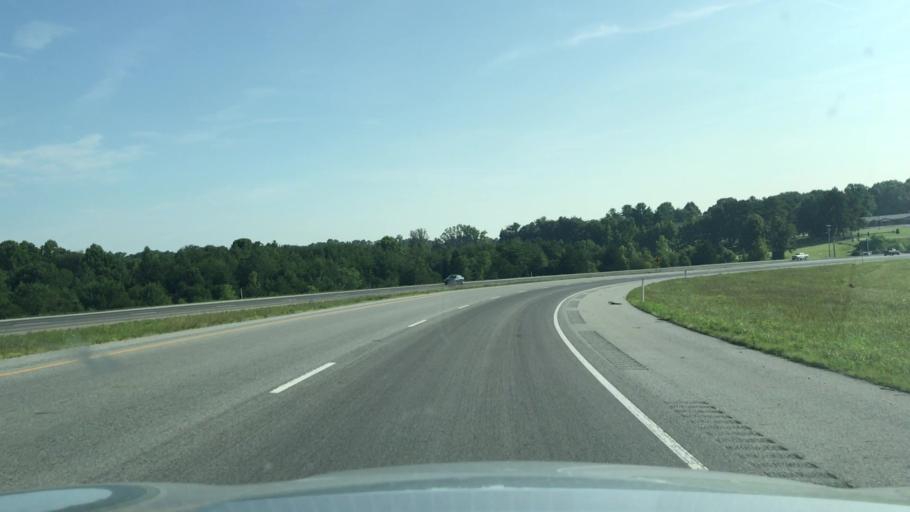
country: US
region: Tennessee
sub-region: Putnam County
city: Algood
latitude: 36.2017
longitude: -85.4603
